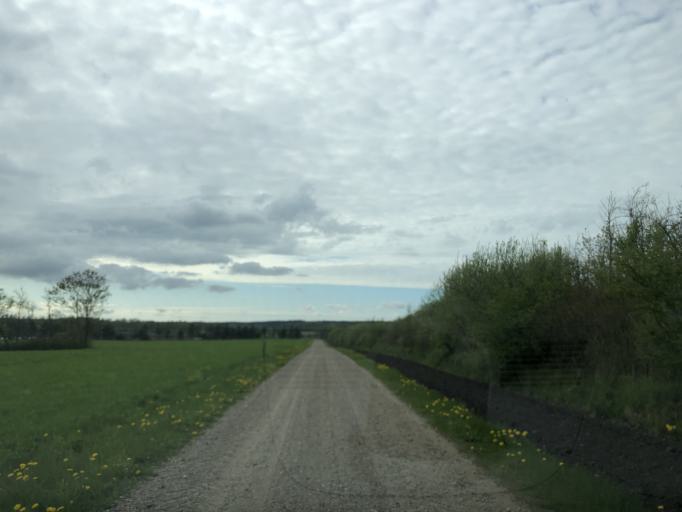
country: DK
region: Central Jutland
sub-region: Holstebro Kommune
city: Ulfborg
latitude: 56.1926
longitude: 8.4697
